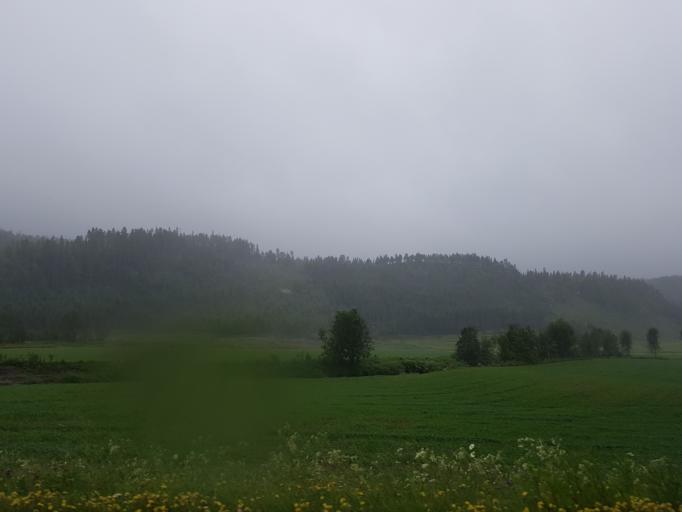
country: NO
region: Nord-Trondelag
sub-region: Stjordal
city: Stjordalshalsen
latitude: 63.3930
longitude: 10.9698
